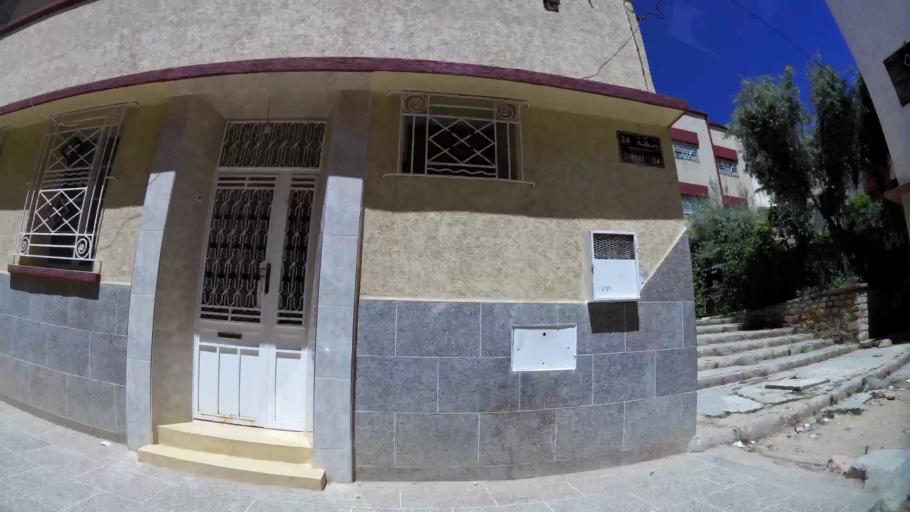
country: MA
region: Meknes-Tafilalet
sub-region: Meknes
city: Meknes
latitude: 33.8786
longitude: -5.5650
